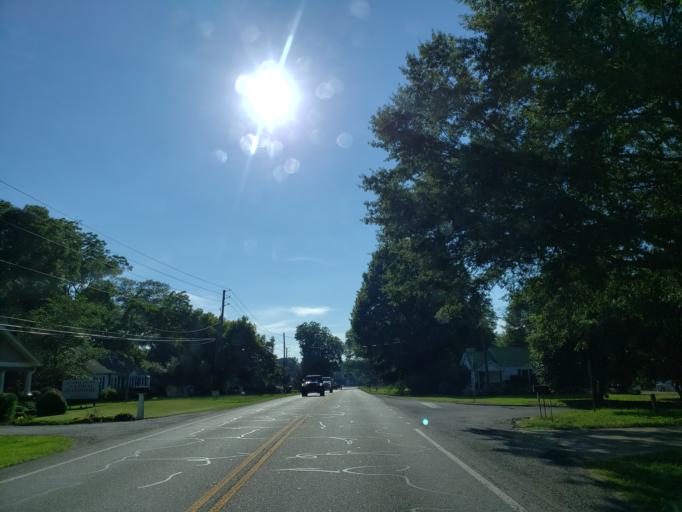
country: US
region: Georgia
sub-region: Fulton County
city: Milton
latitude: 34.2469
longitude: -84.3028
